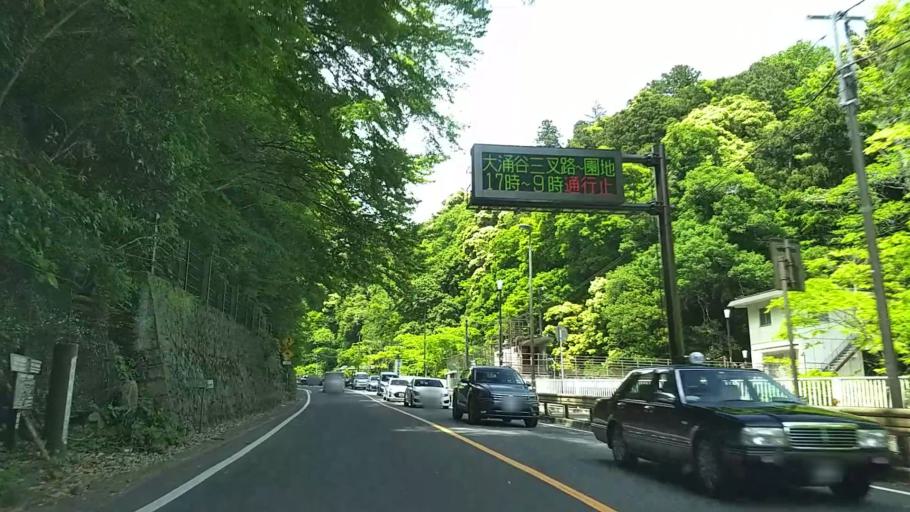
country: JP
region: Kanagawa
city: Odawara
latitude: 35.2323
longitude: 139.0990
